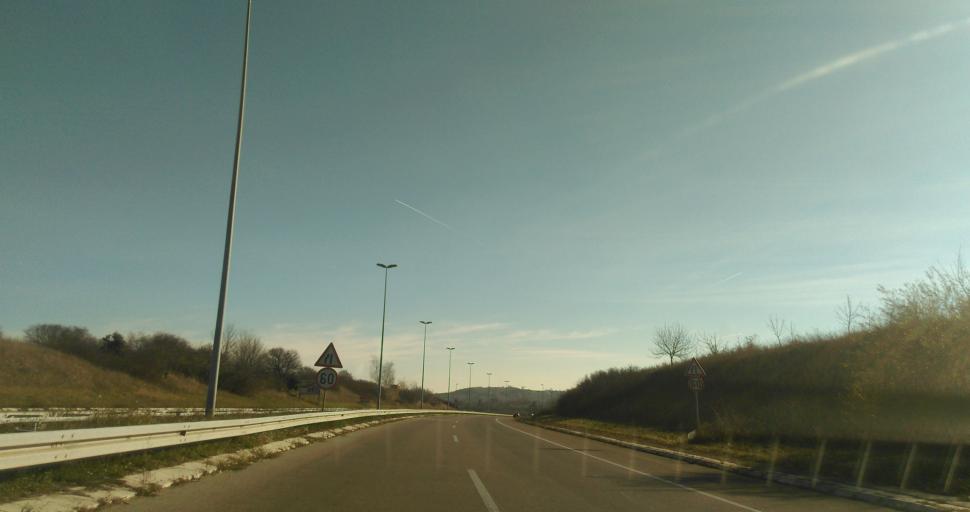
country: RS
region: Autonomna Pokrajina Vojvodina
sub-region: Juznobacki Okrug
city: Petrovaradin
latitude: 45.2268
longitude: 19.8674
